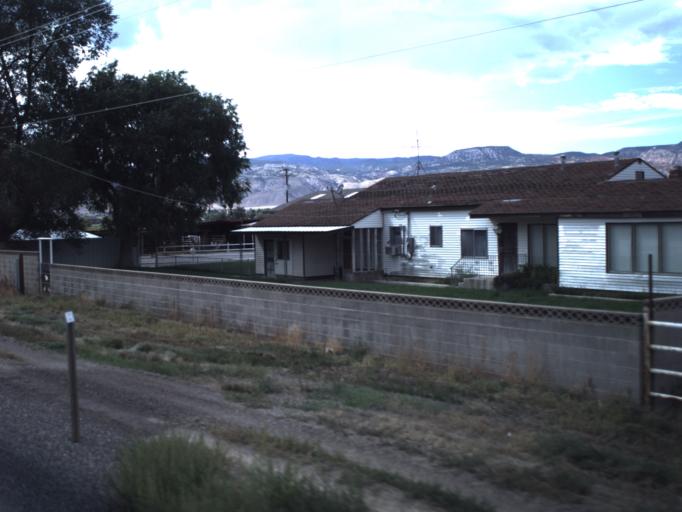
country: US
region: Utah
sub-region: Sevier County
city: Richfield
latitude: 38.7736
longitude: -112.0348
